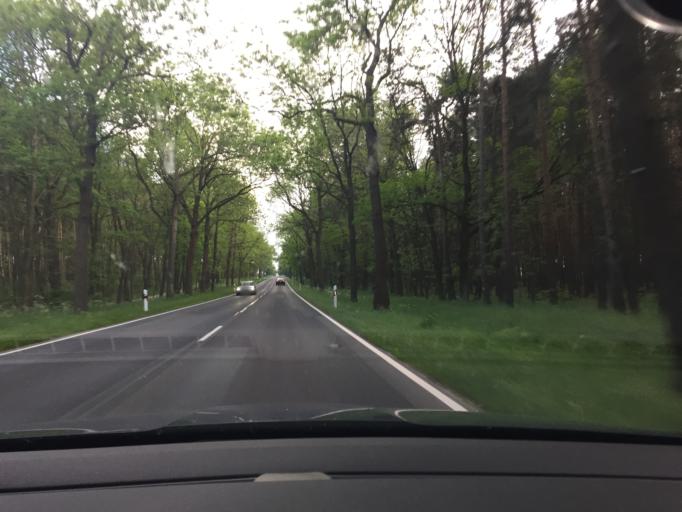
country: DE
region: Brandenburg
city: Treuenbrietzen
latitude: 52.0476
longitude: 12.8148
